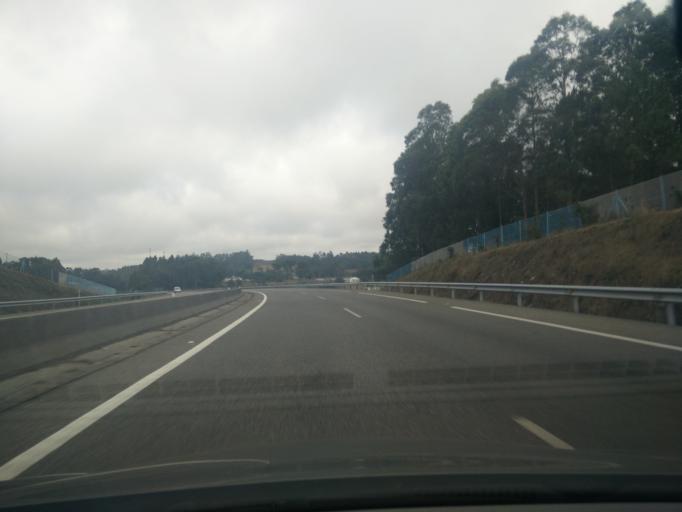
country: ES
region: Galicia
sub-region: Provincia da Coruna
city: Laracha
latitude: 43.2697
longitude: -8.5728
